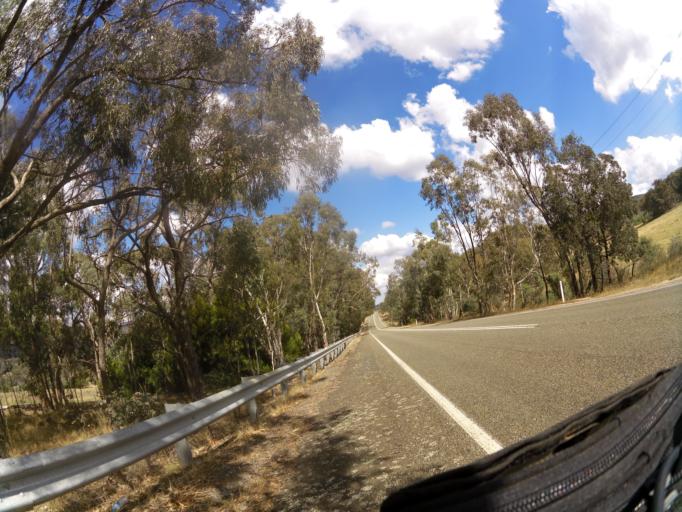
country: AU
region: Victoria
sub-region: Benalla
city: Benalla
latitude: -36.7935
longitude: 146.0108
